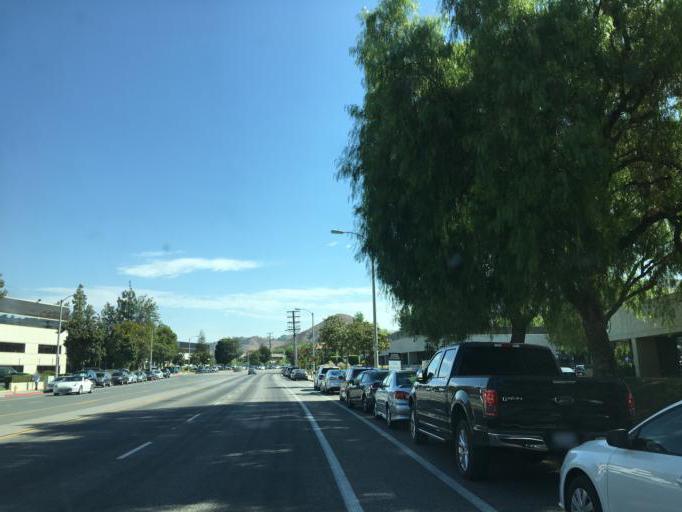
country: US
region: California
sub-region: Los Angeles County
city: Agoura
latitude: 34.1417
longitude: -118.7033
